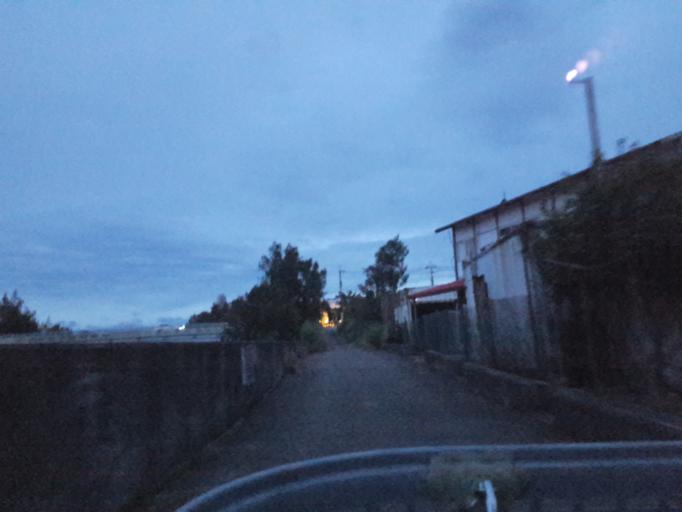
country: TW
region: Taiwan
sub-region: Hsinchu
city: Hsinchu
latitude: 24.7405
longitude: 120.9050
